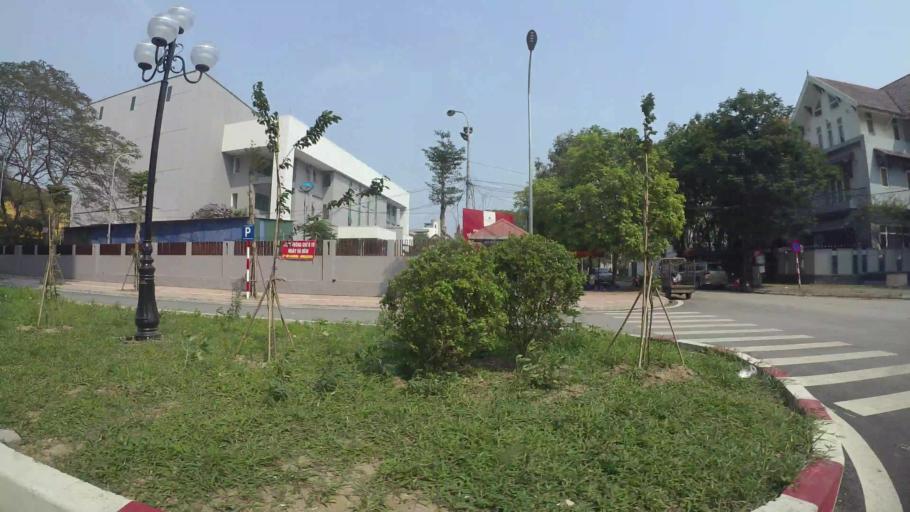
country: VN
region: Ha Noi
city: Tay Ho
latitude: 21.0786
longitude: 105.8145
